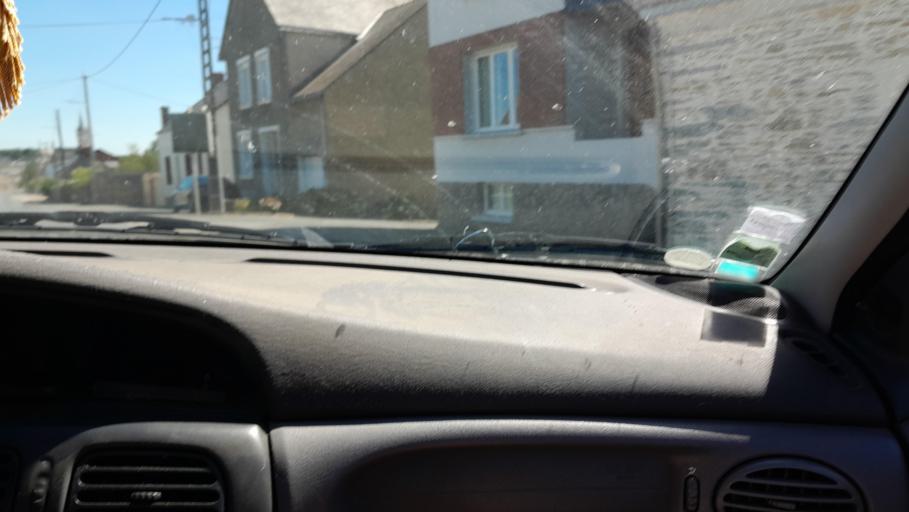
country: FR
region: Pays de la Loire
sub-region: Departement de la Loire-Atlantique
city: Saint-Mars-la-Jaille
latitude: 47.6267
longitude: -1.2000
